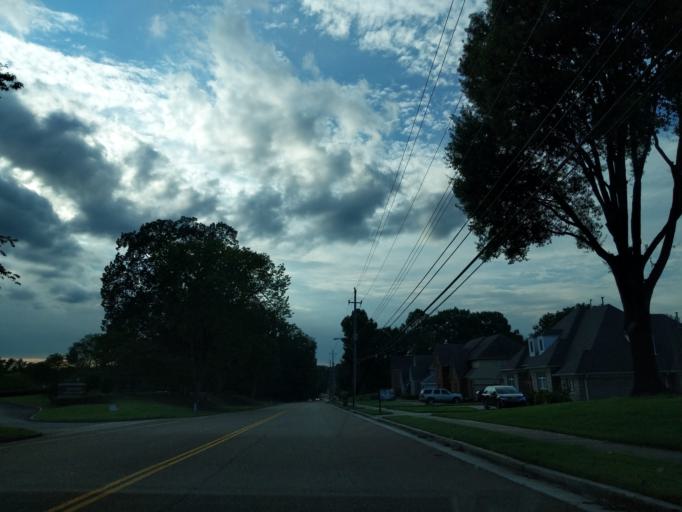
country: US
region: Tennessee
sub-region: Shelby County
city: Germantown
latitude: 35.0674
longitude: -89.7716
